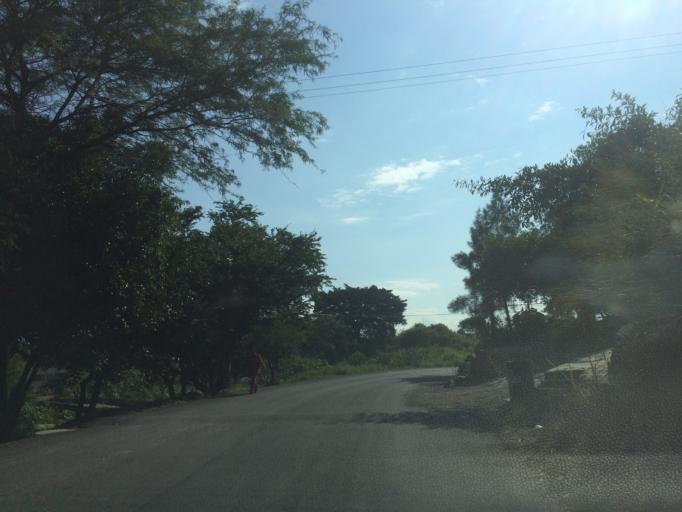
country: MX
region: Nayarit
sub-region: Ahuacatlan
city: Ahuacatlan
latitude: 21.0512
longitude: -104.4751
